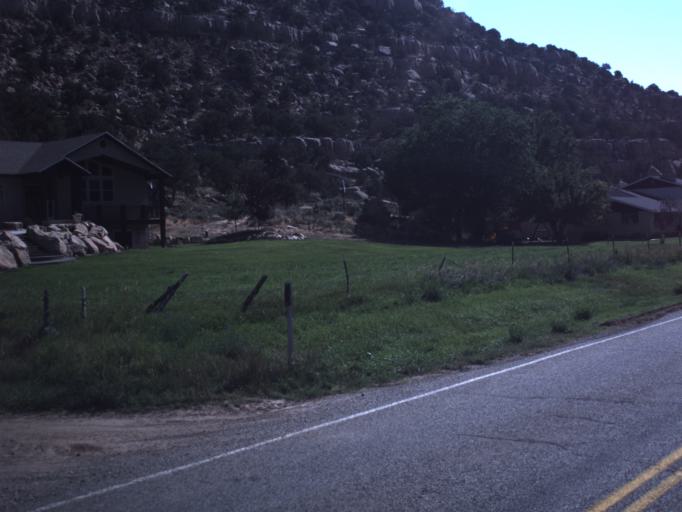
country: US
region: Utah
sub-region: Duchesne County
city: Duchesne
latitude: 40.3174
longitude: -110.6515
